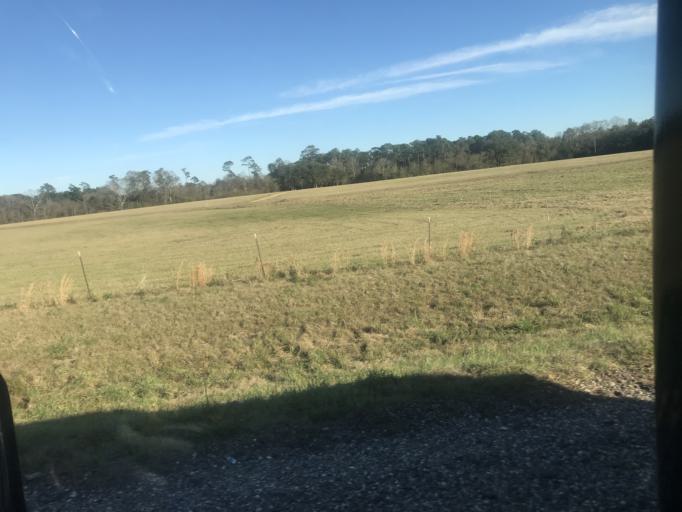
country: US
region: Louisiana
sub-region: Washington Parish
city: Franklinton
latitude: 30.6631
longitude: -90.2035
